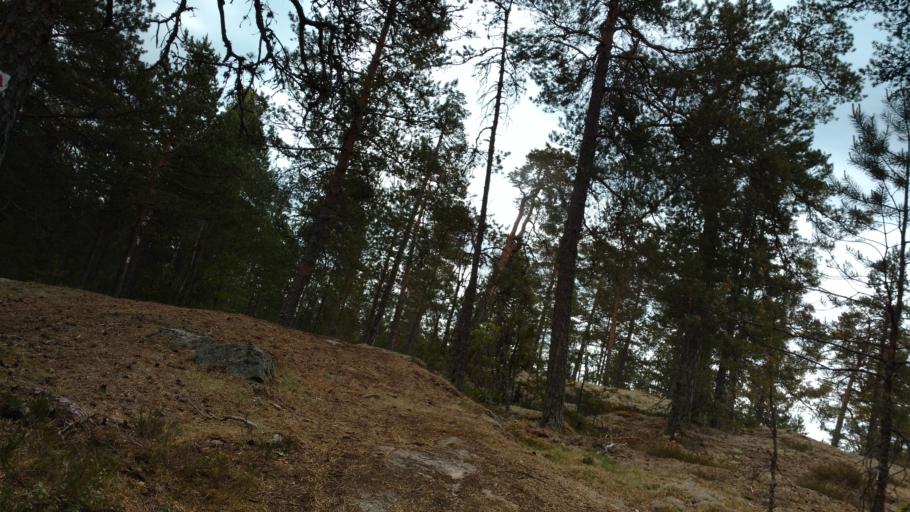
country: FI
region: Uusimaa
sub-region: Raaseporin
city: Pohja
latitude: 60.1106
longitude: 23.5534
